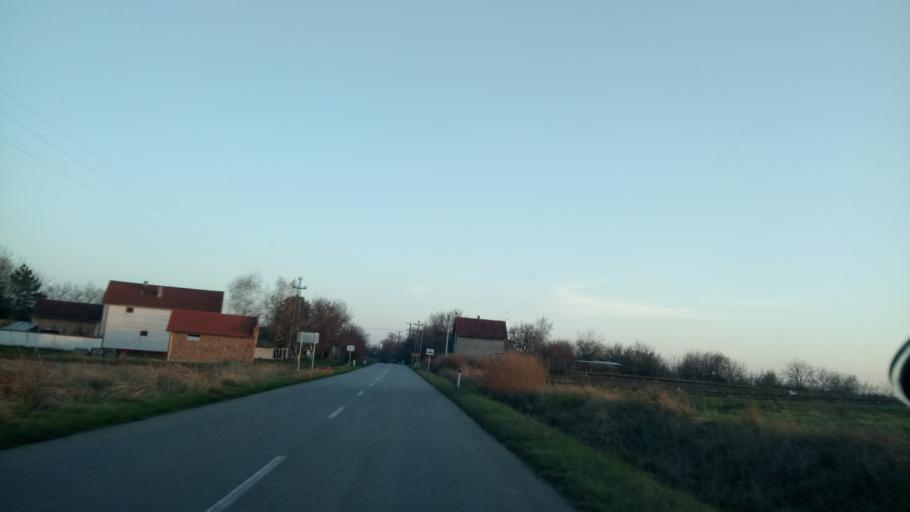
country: RS
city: Surduk
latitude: 45.0844
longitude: 20.3068
